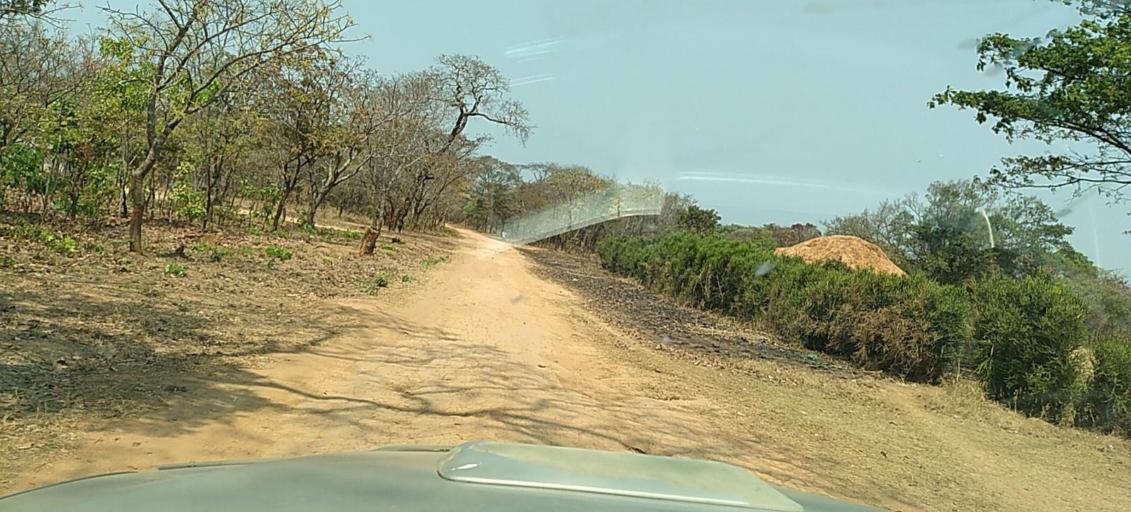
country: ZM
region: North-Western
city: Kasempa
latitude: -13.6682
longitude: 26.2913
